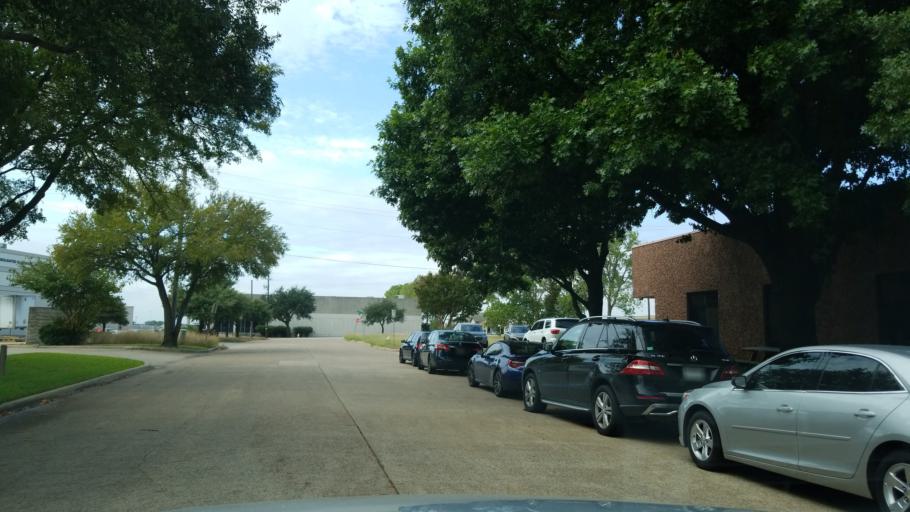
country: US
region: Texas
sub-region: Dallas County
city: Garland
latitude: 32.9009
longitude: -96.6927
